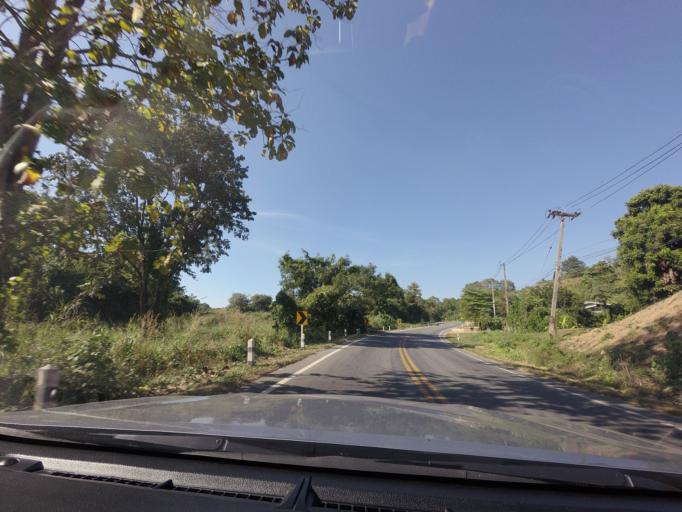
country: TH
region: Sukhothai
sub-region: Amphoe Si Satchanalai
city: Si Satchanalai
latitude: 17.6207
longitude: 99.7055
